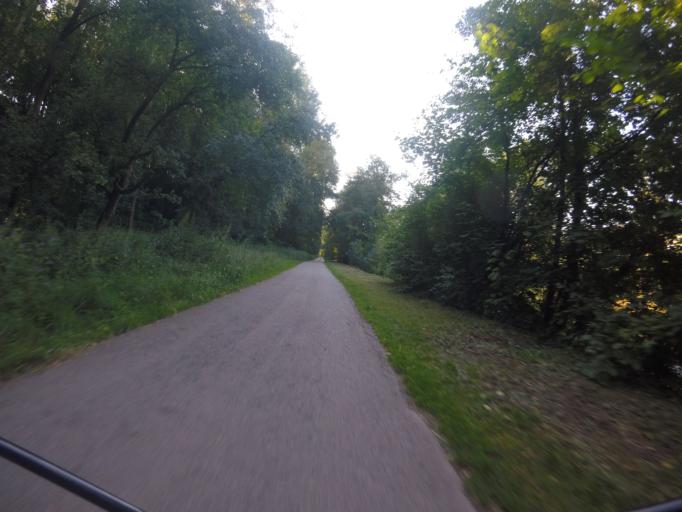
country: DE
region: Baden-Wuerttemberg
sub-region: Regierungsbezirk Stuttgart
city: Steinheim am der Murr
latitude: 48.9622
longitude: 9.2837
